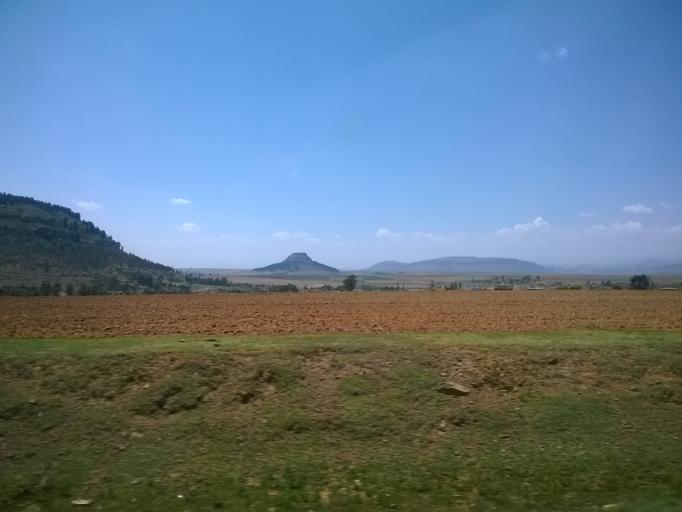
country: LS
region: Leribe
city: Maputsoe
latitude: -28.9587
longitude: 27.9613
